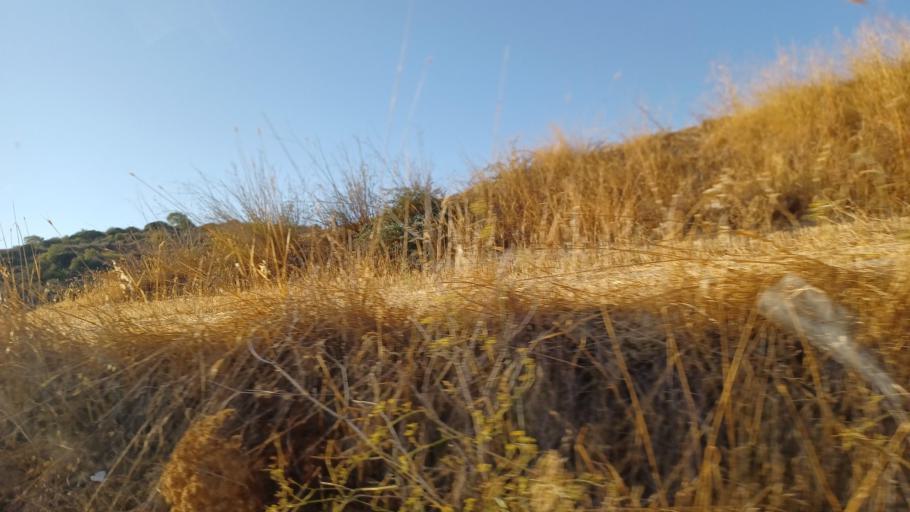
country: CY
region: Pafos
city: Polis
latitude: 34.9773
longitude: 32.4549
